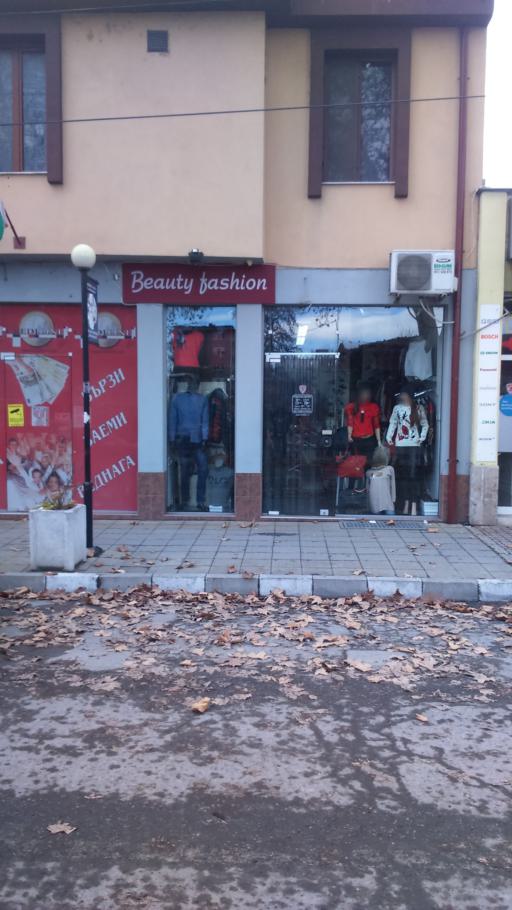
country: BG
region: Plovdiv
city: Stamboliyski
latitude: 42.1327
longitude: 24.5350
